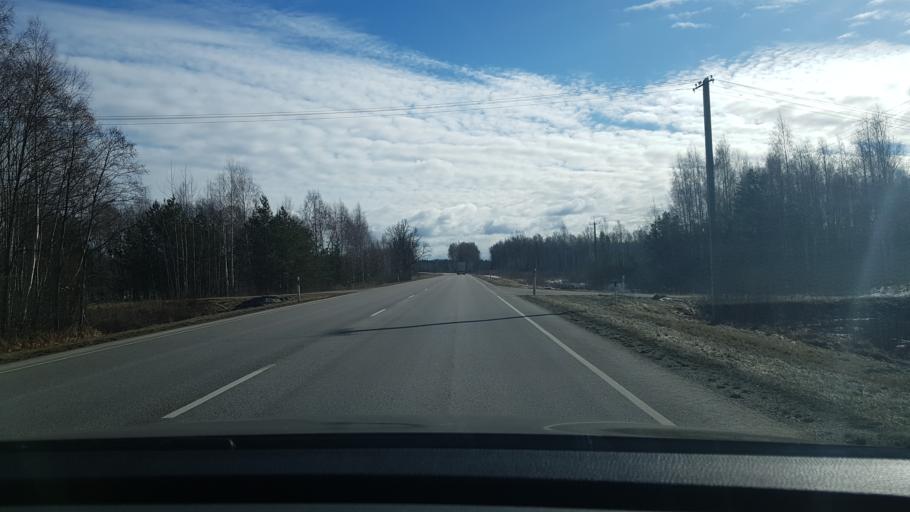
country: EE
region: Paernumaa
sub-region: Saarde vald
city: Kilingi-Nomme
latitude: 58.1771
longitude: 24.8025
